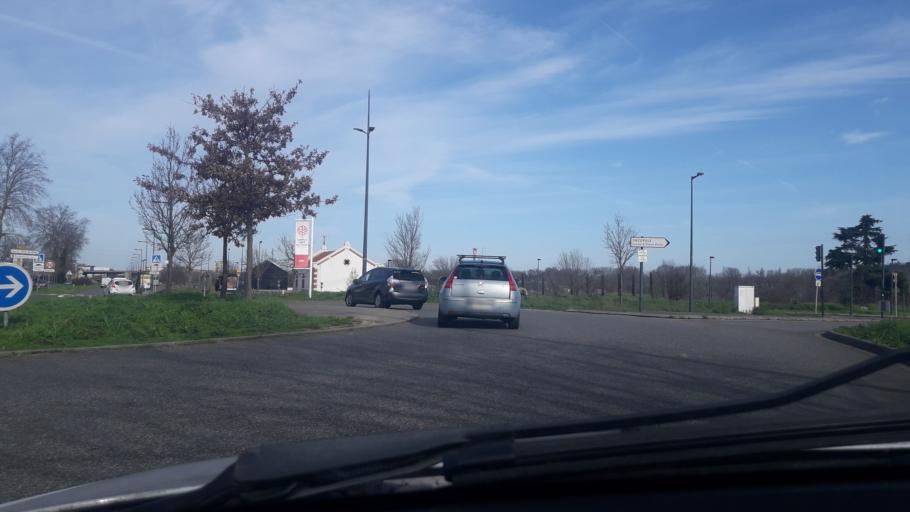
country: FR
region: Midi-Pyrenees
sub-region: Departement de la Haute-Garonne
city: Vieille-Toulouse
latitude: 43.5627
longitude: 1.4253
